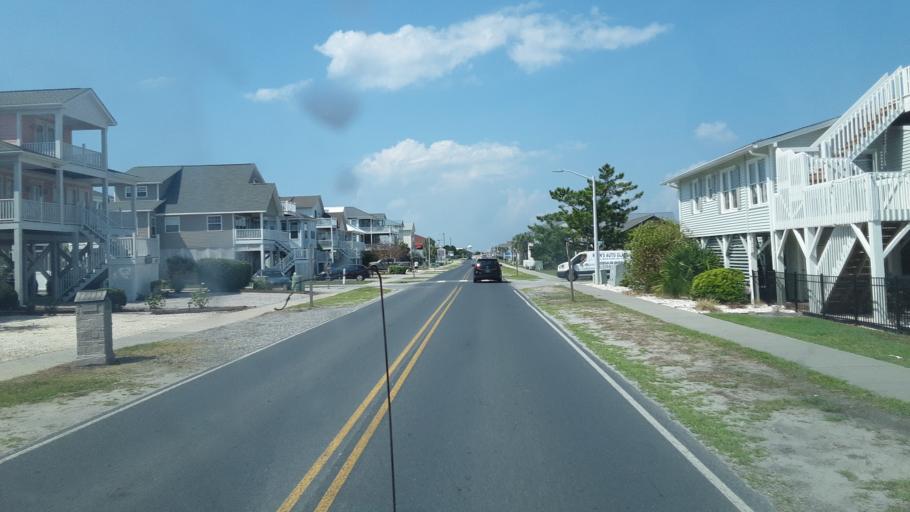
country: US
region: North Carolina
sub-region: Brunswick County
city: Sunset Beach
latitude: 33.8894
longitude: -78.4325
